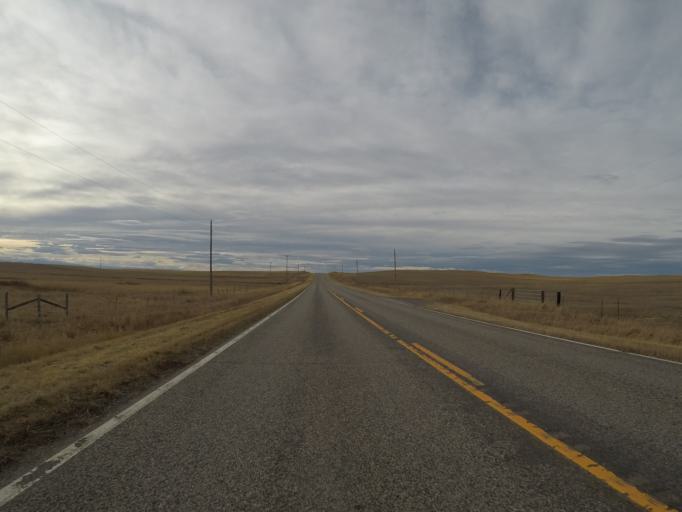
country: US
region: Montana
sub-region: Yellowstone County
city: Laurel
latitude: 45.8563
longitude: -108.7899
